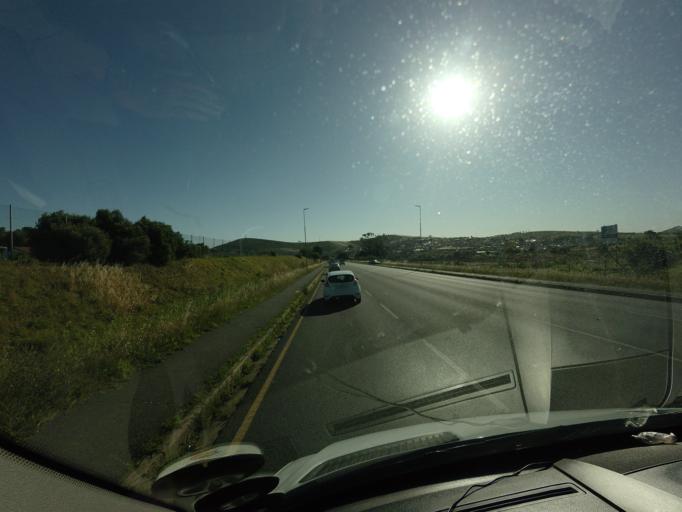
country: ZA
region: Western Cape
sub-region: Cape Winelands District Municipality
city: Stellenbosch
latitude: -33.9220
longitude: 18.8612
